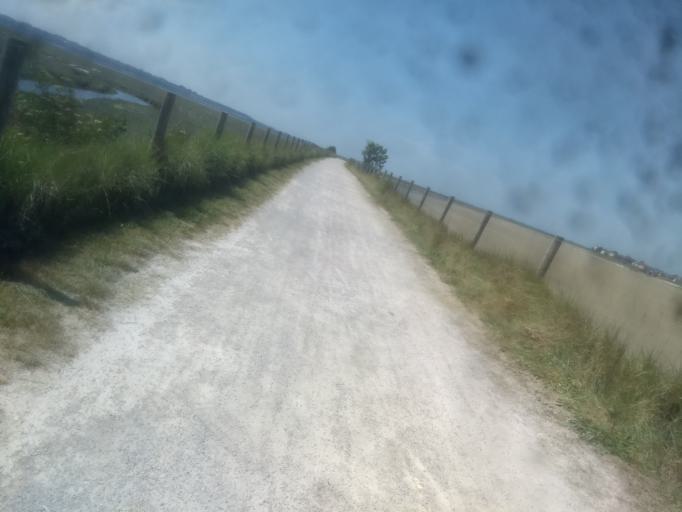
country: FR
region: Picardie
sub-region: Departement de la Somme
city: Le Crotoy
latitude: 50.2148
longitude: 1.6484
